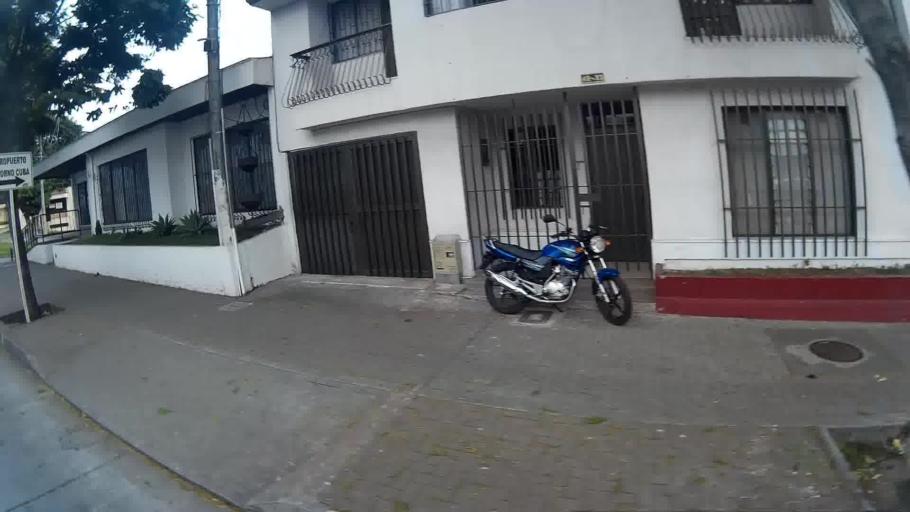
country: CO
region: Risaralda
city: Pereira
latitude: 4.8158
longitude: -75.7191
